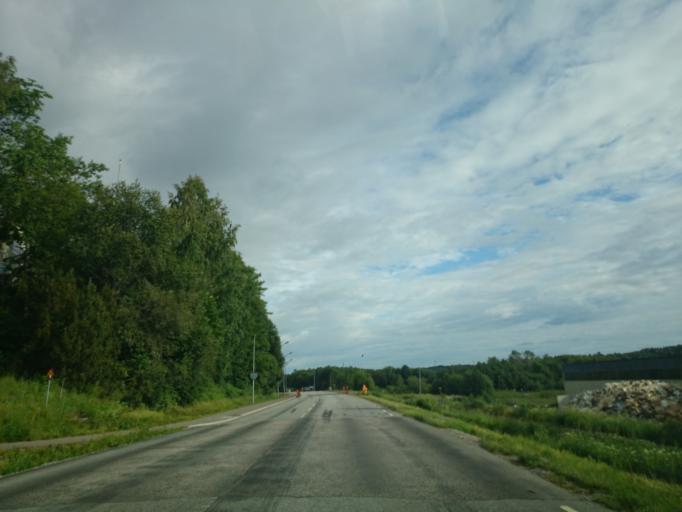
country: SE
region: Vaesternorrland
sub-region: Sundsvalls Kommun
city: Johannedal
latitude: 62.4406
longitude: 17.3852
